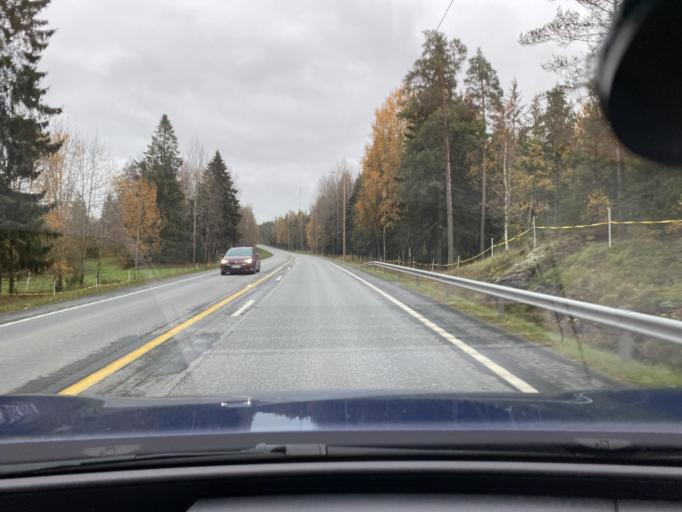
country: FI
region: Varsinais-Suomi
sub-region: Vakka-Suomi
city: Laitila
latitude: 60.9355
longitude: 21.6046
